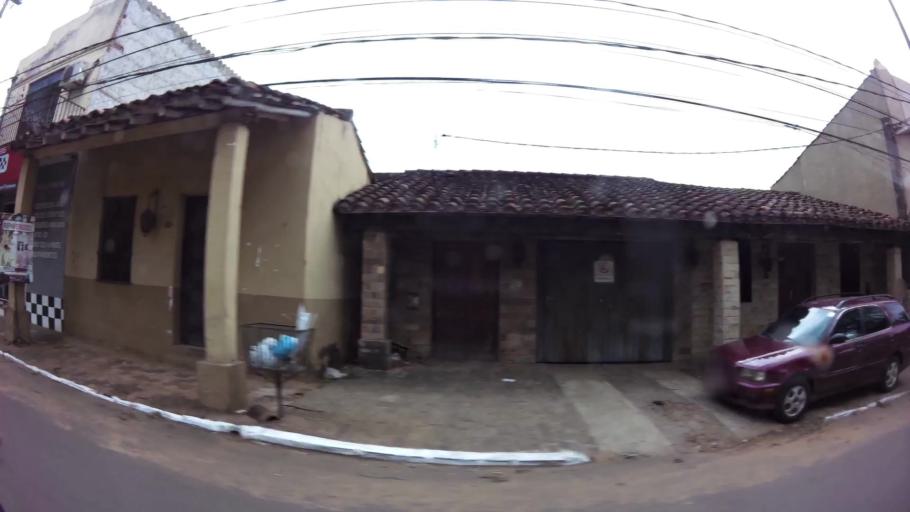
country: PY
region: Central
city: San Lorenzo
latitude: -25.2666
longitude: -57.4923
